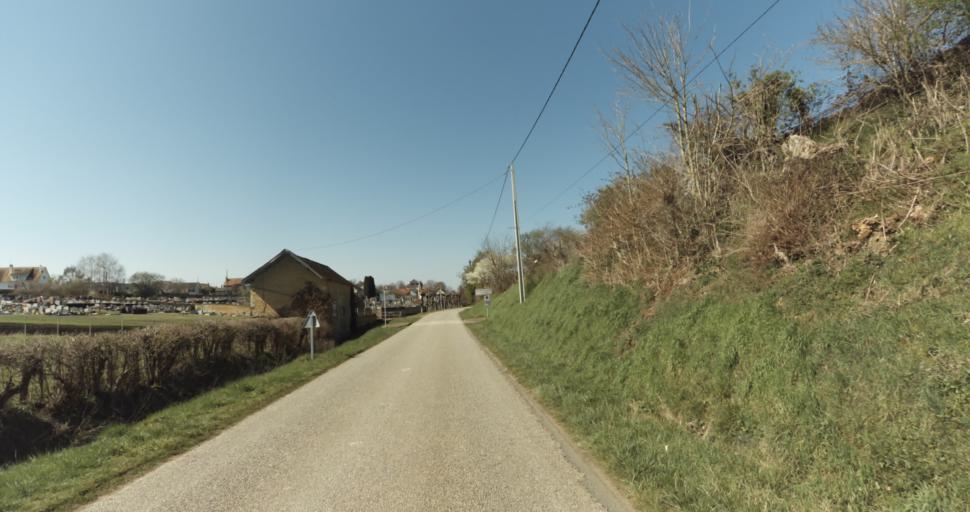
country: FR
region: Lower Normandy
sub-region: Departement du Calvados
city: Saint-Pierre-sur-Dives
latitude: 49.0168
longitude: -0.0243
